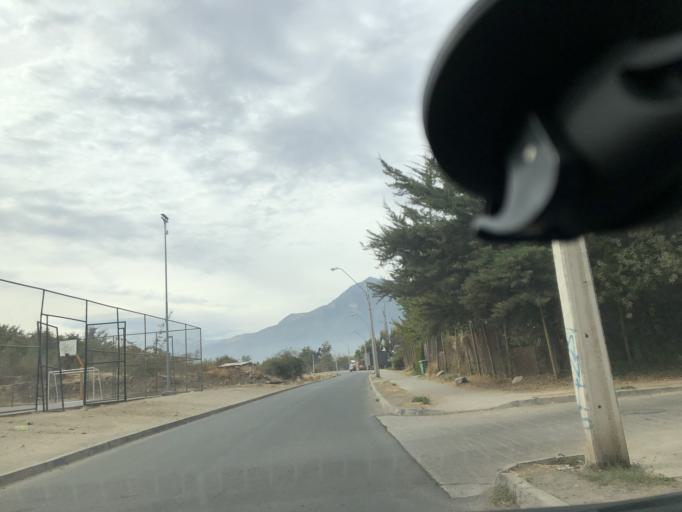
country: CL
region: Santiago Metropolitan
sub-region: Provincia de Cordillera
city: Puente Alto
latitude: -33.6069
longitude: -70.5335
